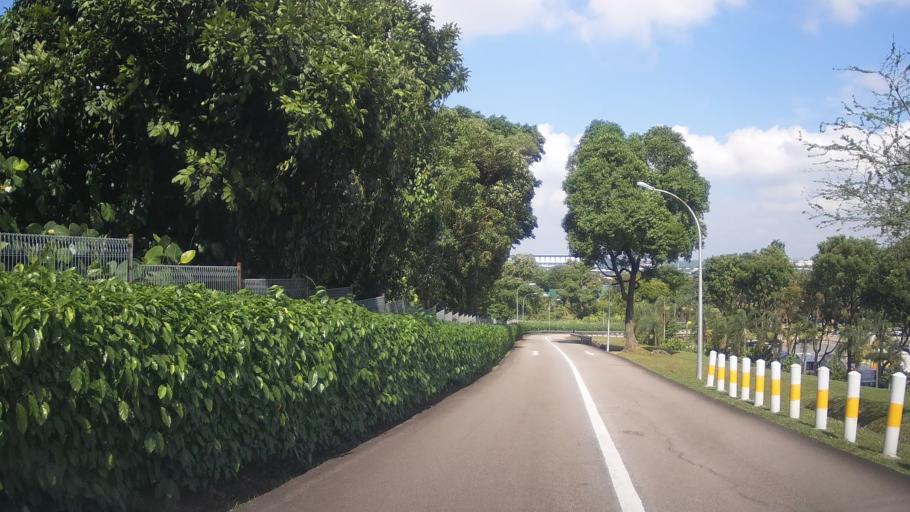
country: SG
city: Singapore
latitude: 1.3197
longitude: 103.7087
